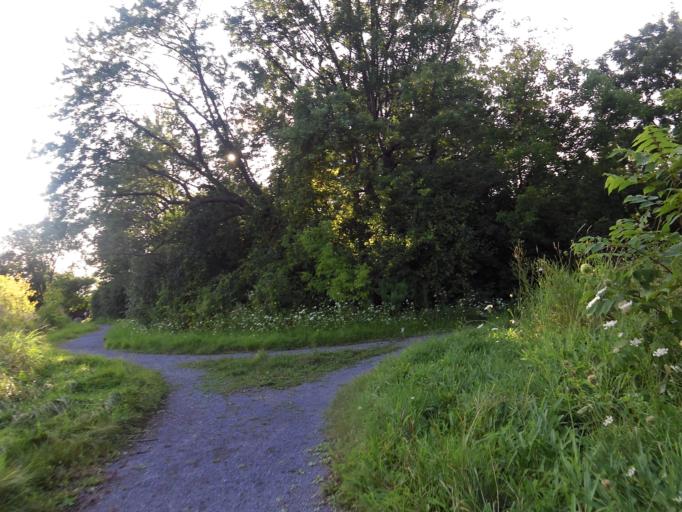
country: CA
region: Ontario
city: Ottawa
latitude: 45.3662
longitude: -75.6967
